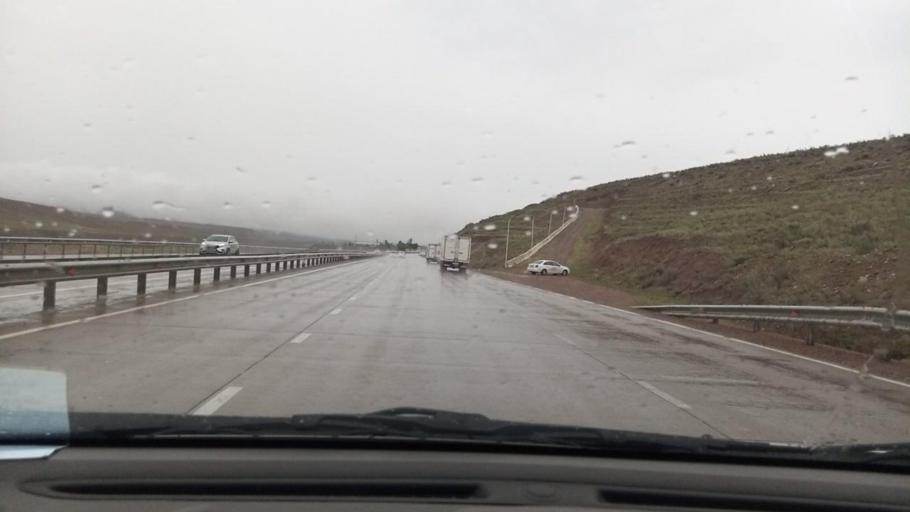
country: UZ
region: Namangan
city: Pop Shahri
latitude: 40.9260
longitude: 70.7213
